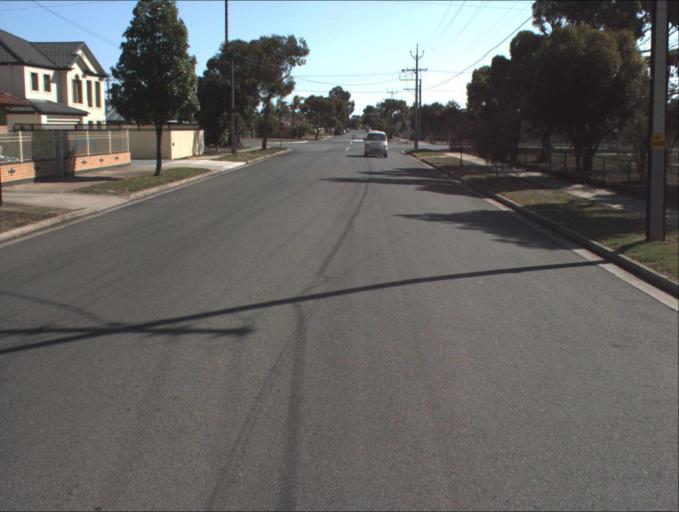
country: AU
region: South Australia
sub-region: Port Adelaide Enfield
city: Alberton
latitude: -34.8485
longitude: 138.5364
